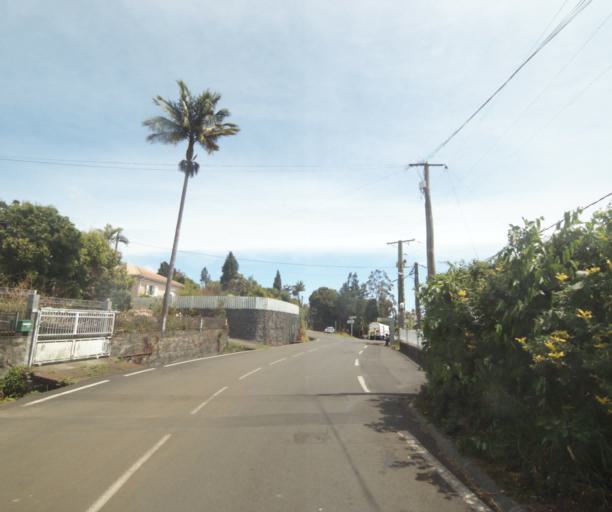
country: RE
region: Reunion
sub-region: Reunion
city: Trois-Bassins
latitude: -21.0637
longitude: 55.3080
